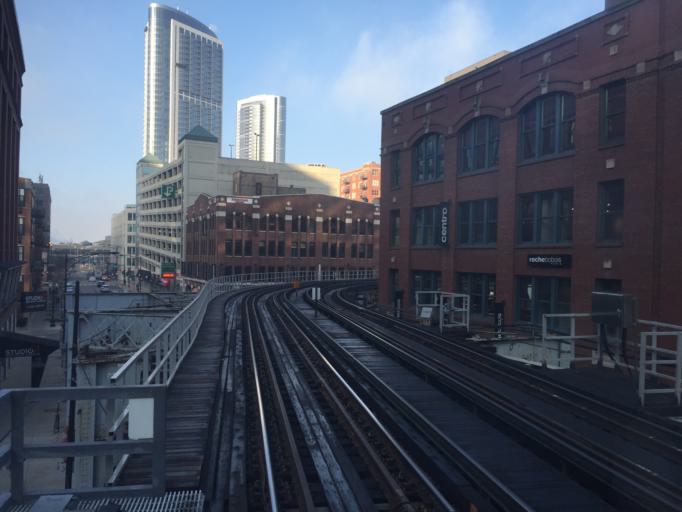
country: US
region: Illinois
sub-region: Cook County
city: Chicago
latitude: 41.8901
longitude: -87.6348
